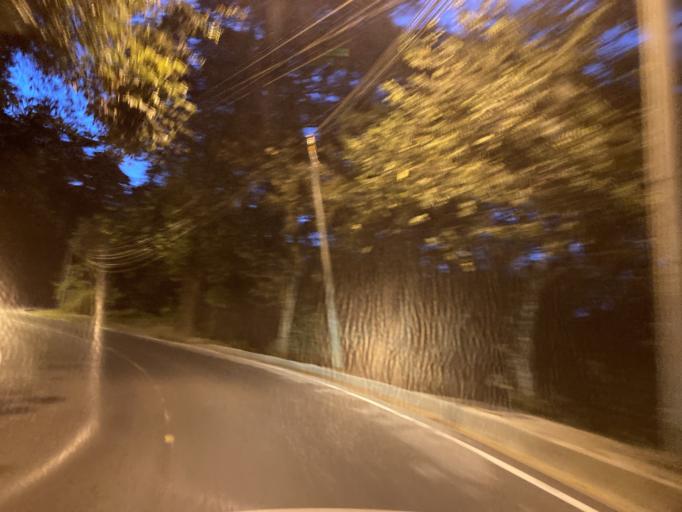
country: GT
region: Guatemala
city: Santa Catarina Pinula
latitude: 14.5952
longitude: -90.4644
